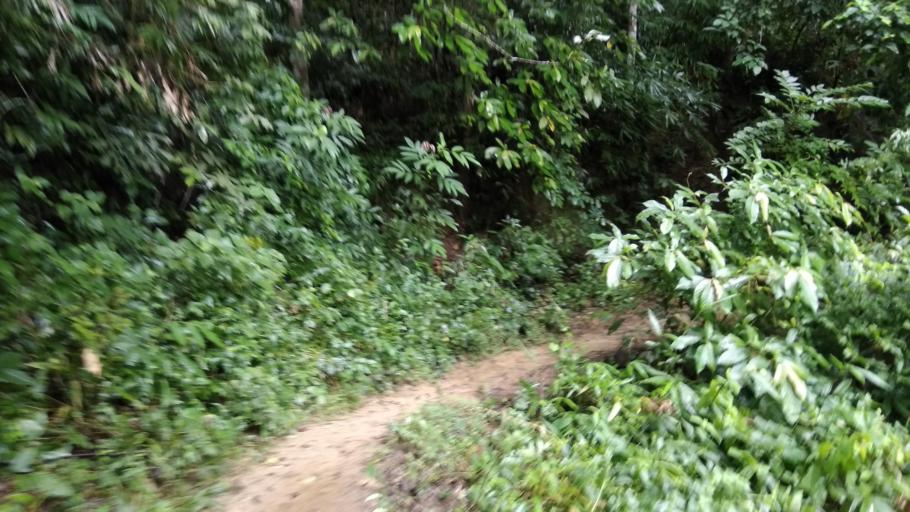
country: IN
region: Tripura
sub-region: Dhalai
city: Kamalpur
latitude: 24.1732
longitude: 91.8878
